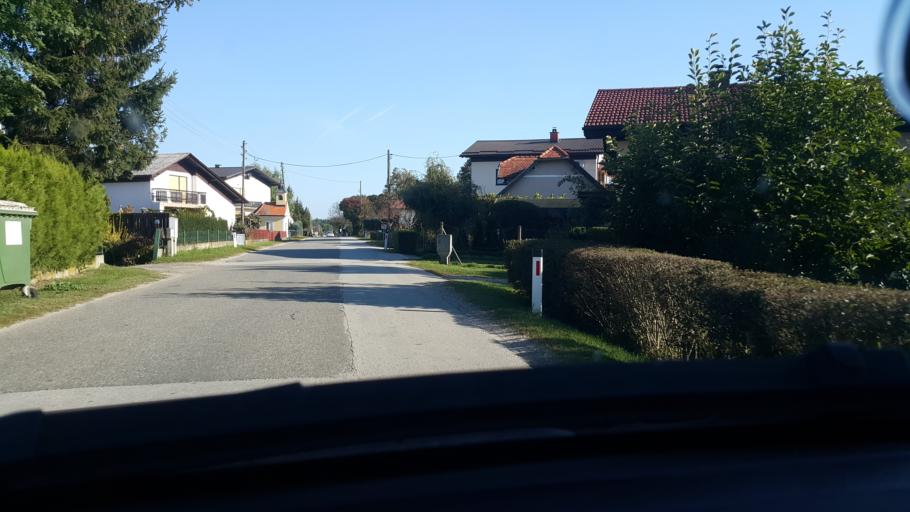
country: SI
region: Race-Fram
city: Race
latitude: 46.4390
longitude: 15.7261
